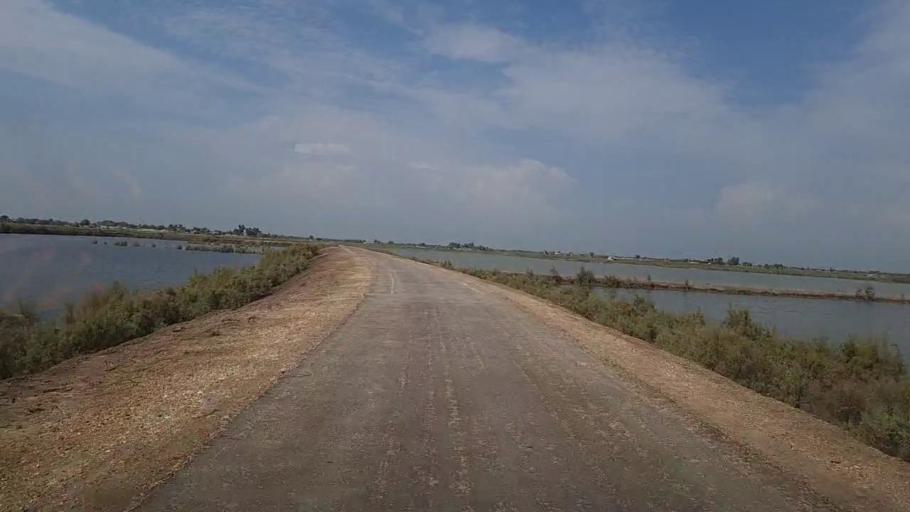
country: PK
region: Sindh
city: Thul
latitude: 28.2833
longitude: 68.8231
